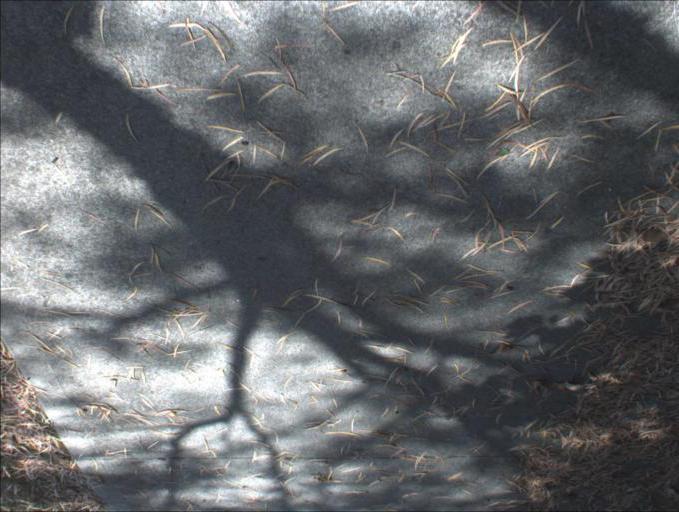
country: AU
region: Queensland
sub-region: Logan
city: Windaroo
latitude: -27.7496
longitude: 153.1909
